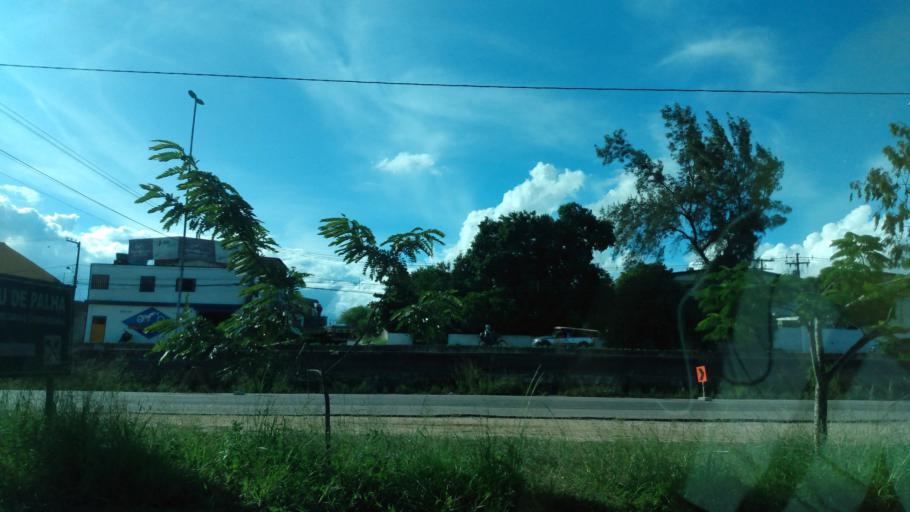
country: ET
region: Oromiya
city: Gore
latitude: 8.1967
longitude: 35.5738
